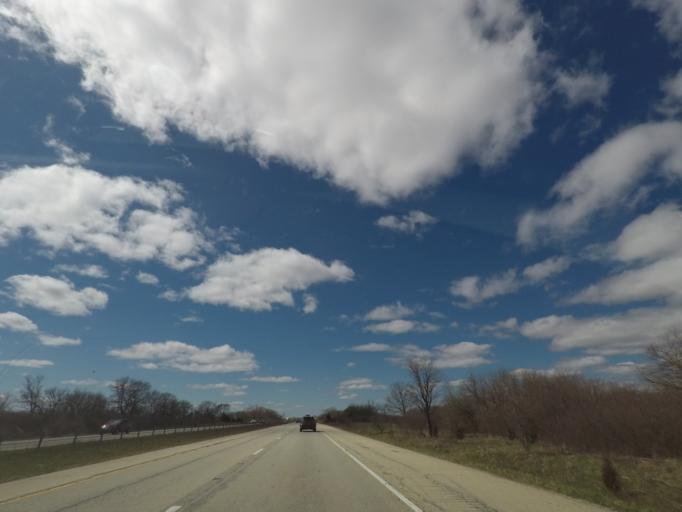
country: US
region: Illinois
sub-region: Grundy County
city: Central City
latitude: 41.2127
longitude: -88.2940
